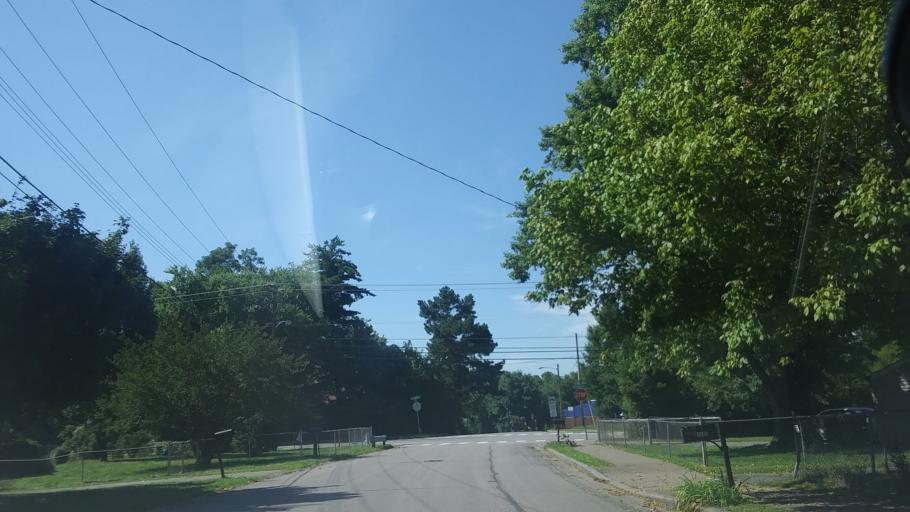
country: US
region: Tennessee
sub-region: Rutherford County
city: La Vergne
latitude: 36.0686
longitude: -86.6690
